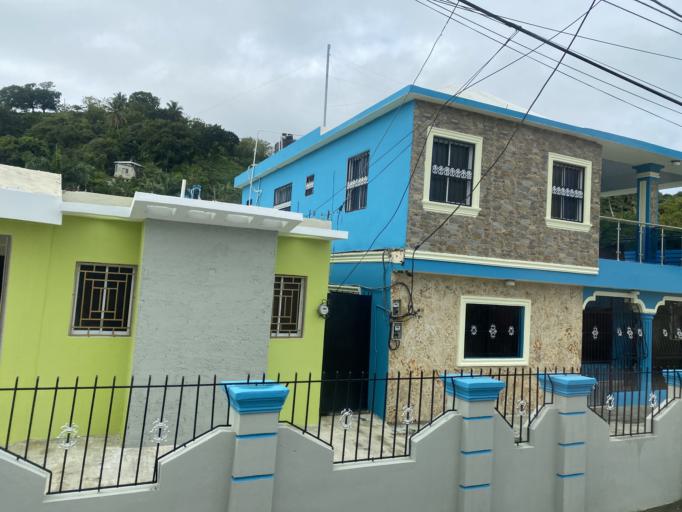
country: DO
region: El Seibo
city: Miches
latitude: 18.9845
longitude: -69.0513
